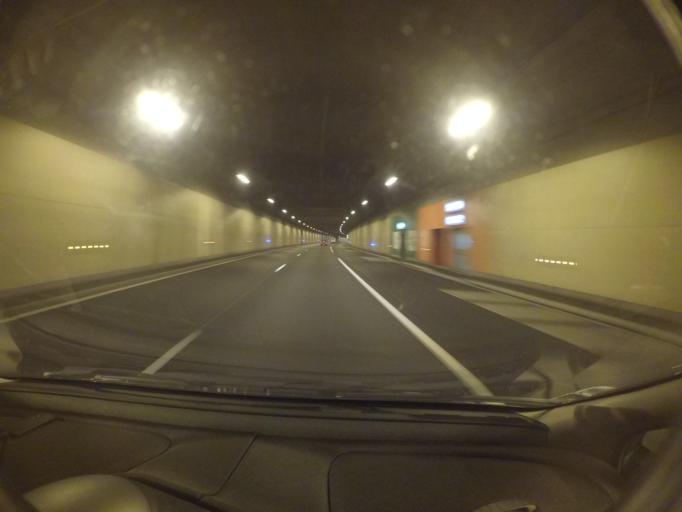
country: FR
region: Pays de la Loire
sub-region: Departement de Maine-et-Loire
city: Avrille
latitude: 47.4904
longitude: -0.5829
